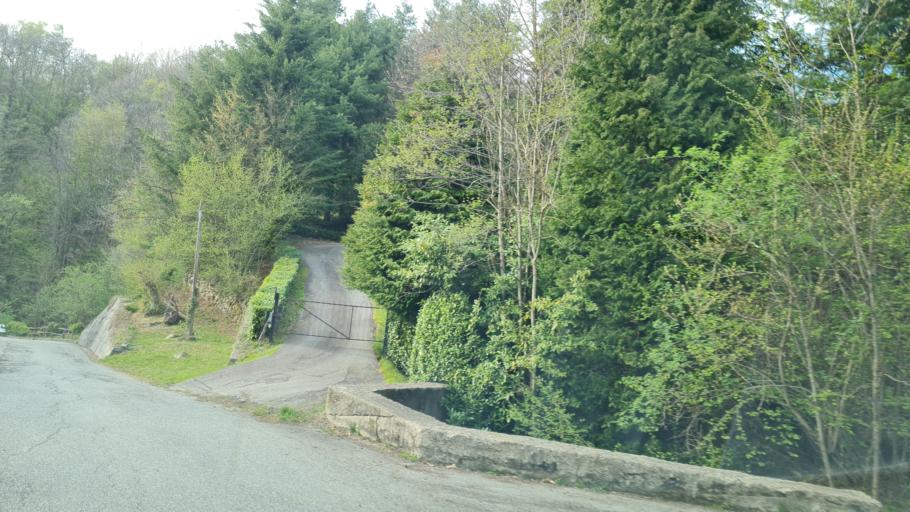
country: IT
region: Piedmont
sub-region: Provincia di Biella
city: Sordevolo
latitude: 45.5794
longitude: 7.9724
